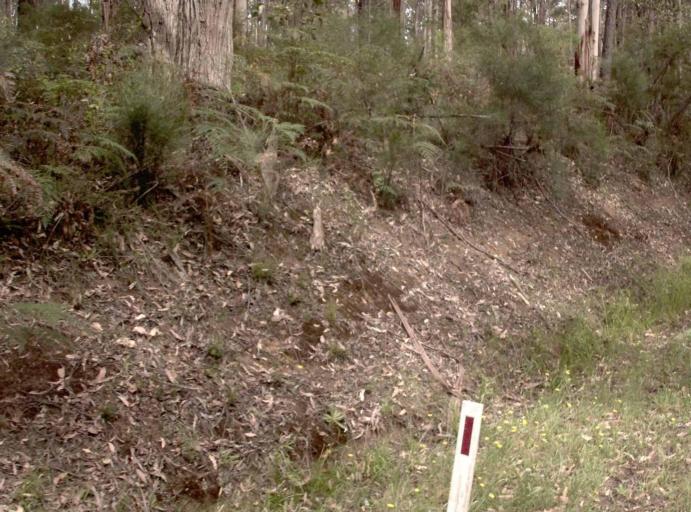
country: AU
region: Victoria
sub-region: Latrobe
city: Moe
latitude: -37.9900
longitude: 146.4087
